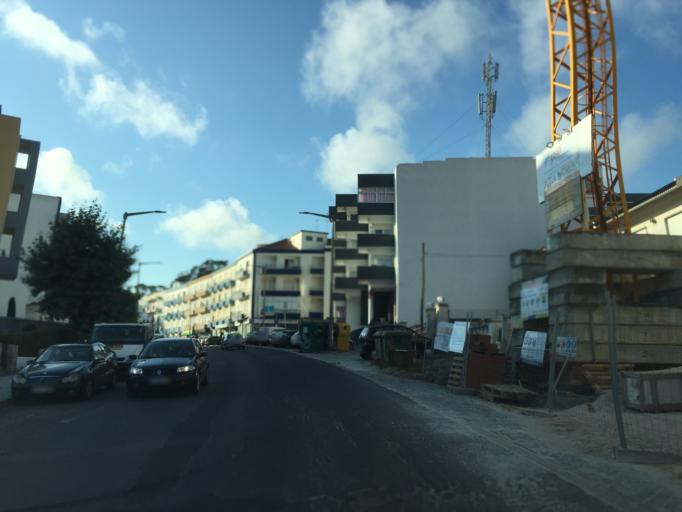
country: PT
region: Leiria
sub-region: Caldas da Rainha
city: Caldas da Rainha
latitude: 39.3983
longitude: -9.1338
